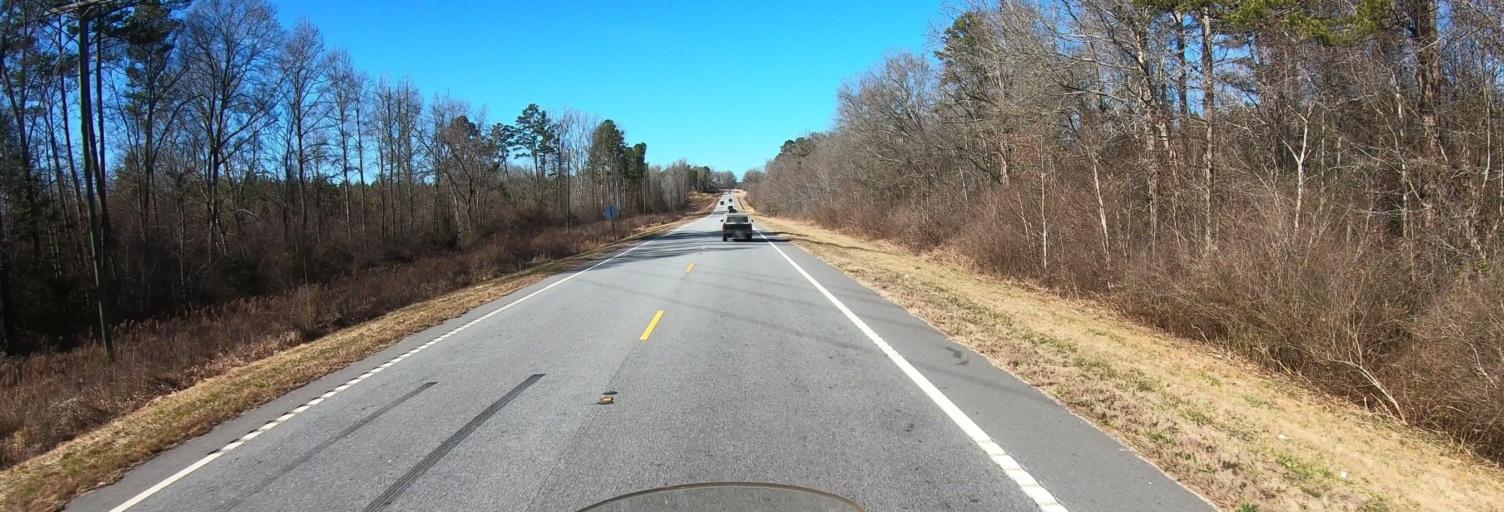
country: US
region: South Carolina
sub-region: Oconee County
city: Walhalla
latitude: 34.7929
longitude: -83.0261
